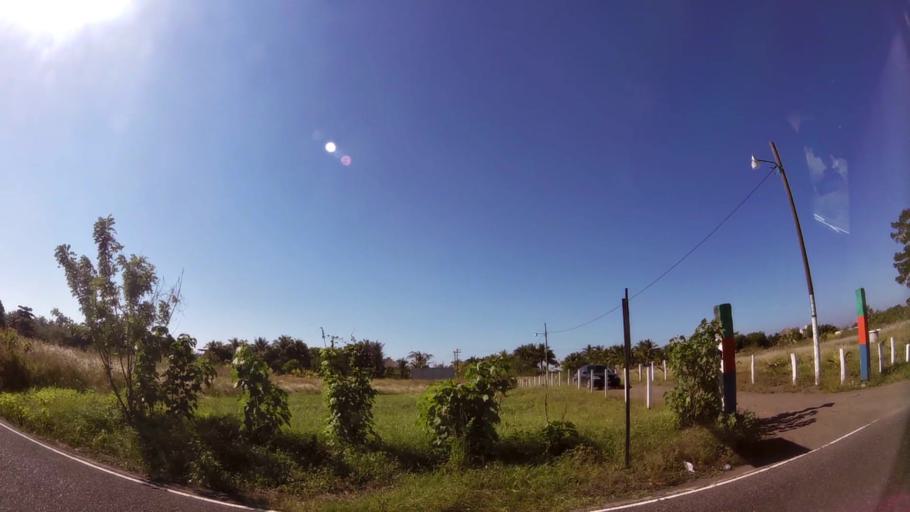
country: GT
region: Santa Rosa
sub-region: Municipio de Taxisco
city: Taxisco
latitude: 13.8687
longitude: -90.4151
